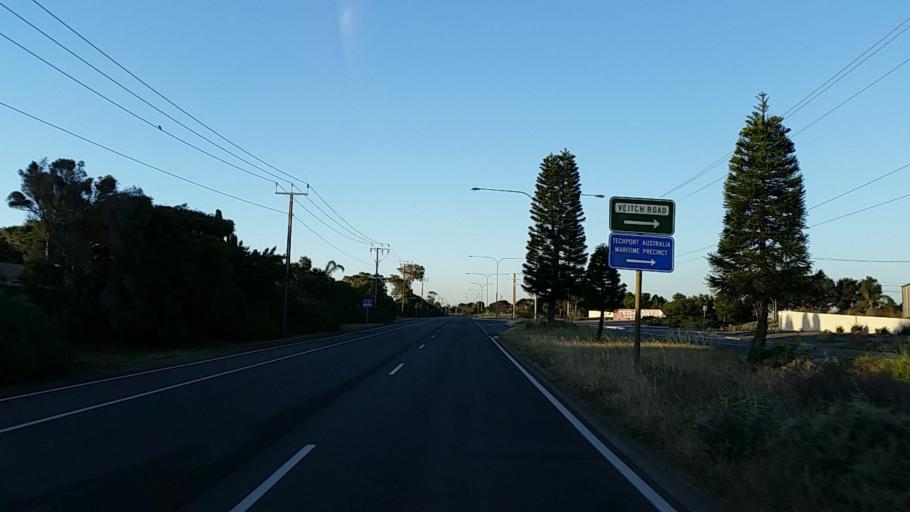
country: AU
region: South Australia
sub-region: Port Adelaide Enfield
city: Birkenhead
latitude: -34.7908
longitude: 138.5014
